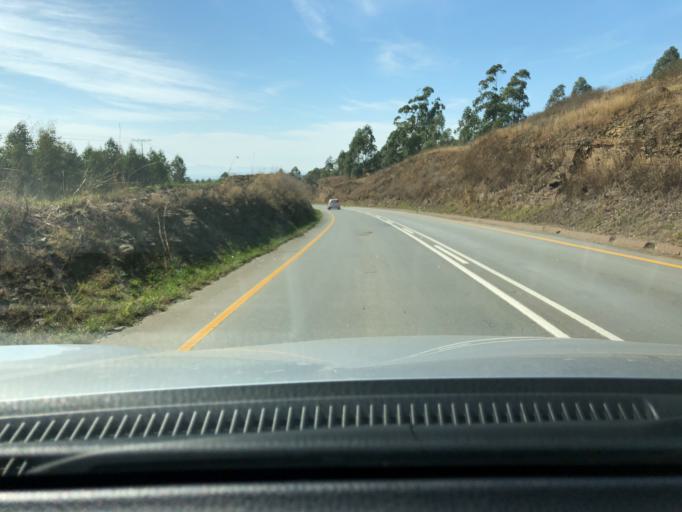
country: ZA
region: KwaZulu-Natal
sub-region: Sisonke District Municipality
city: Ixopo
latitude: -30.1146
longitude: 30.1150
